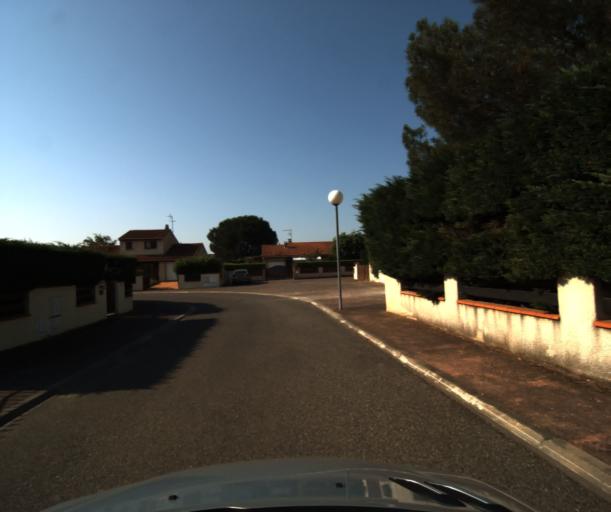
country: FR
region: Midi-Pyrenees
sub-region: Departement de la Haute-Garonne
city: Labarthe-sur-Leze
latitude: 43.4764
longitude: 1.3974
